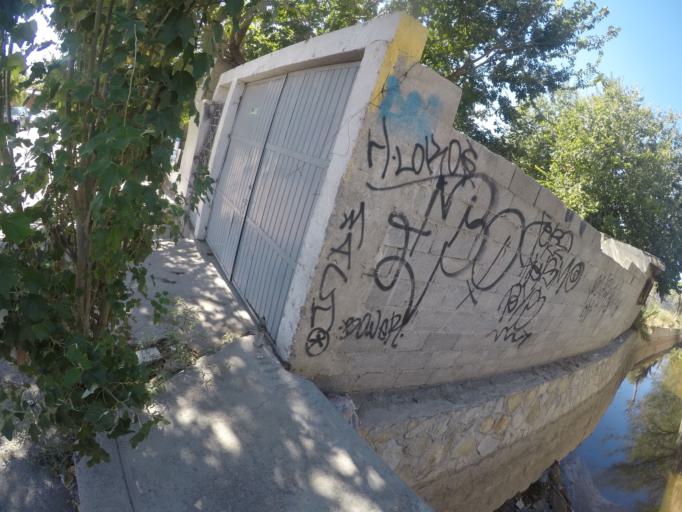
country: MX
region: Chihuahua
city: Ciudad Juarez
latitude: 31.7396
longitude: -106.4673
